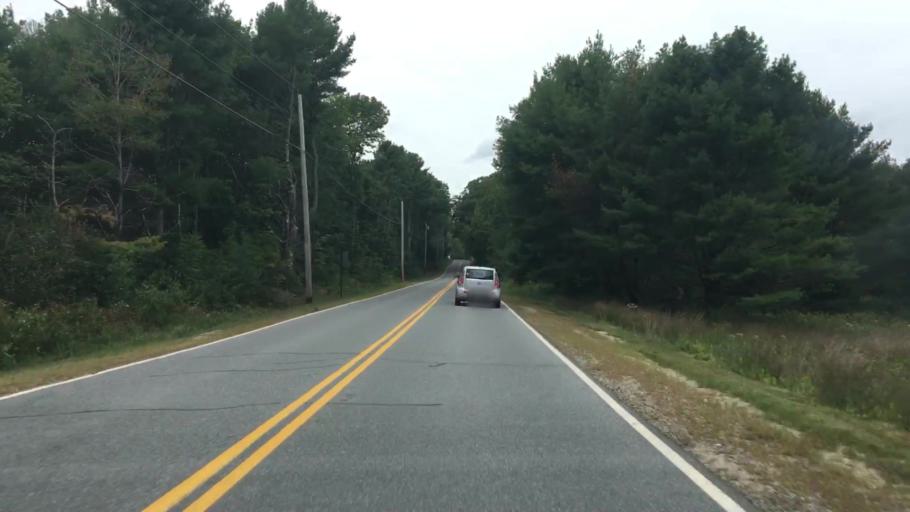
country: US
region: Maine
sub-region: Cumberland County
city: Cumberland Center
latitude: 43.8732
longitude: -70.2373
